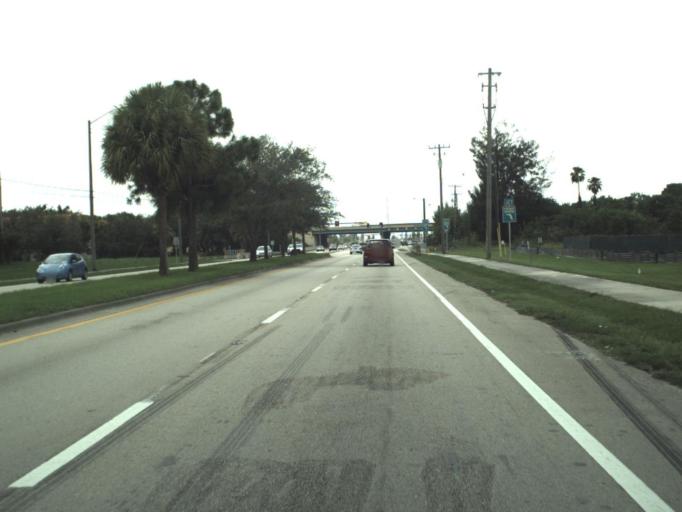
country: US
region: Florida
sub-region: Palm Beach County
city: Villages of Oriole
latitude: 26.4538
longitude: -80.1702
